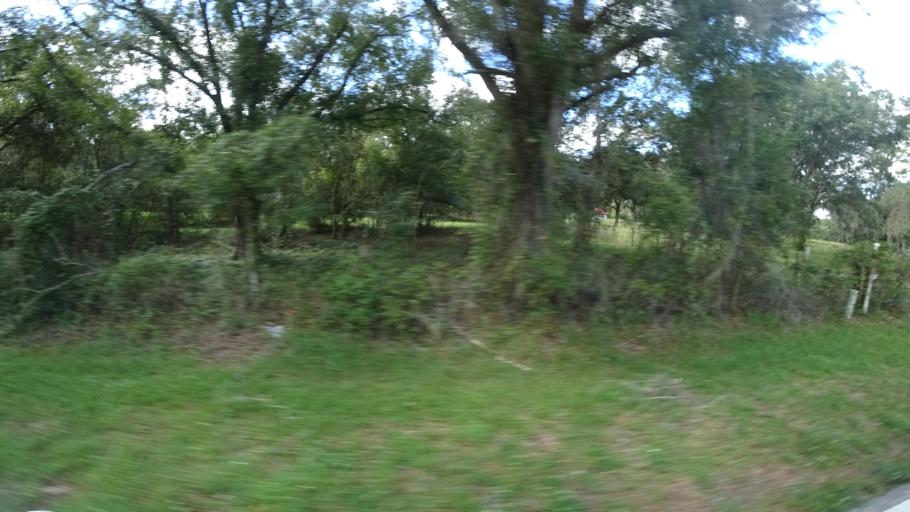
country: US
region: Florida
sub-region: Sarasota County
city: Lake Sarasota
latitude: 27.3249
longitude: -82.2694
